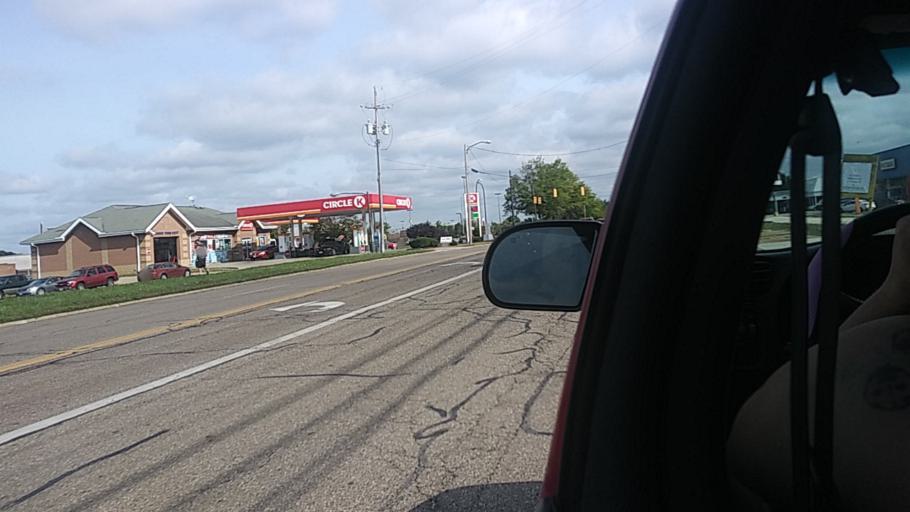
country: US
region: Ohio
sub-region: Summit County
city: Tallmadge
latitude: 41.1098
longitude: -81.4660
